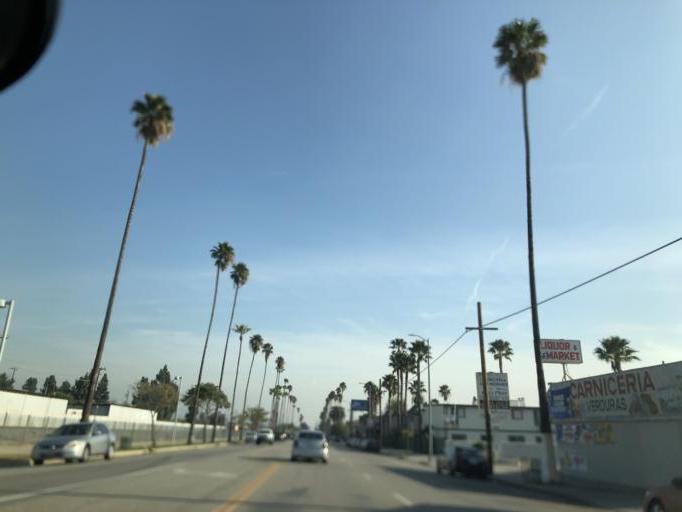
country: US
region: California
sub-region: Los Angeles County
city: San Fernando
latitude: 34.3020
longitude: -118.4630
